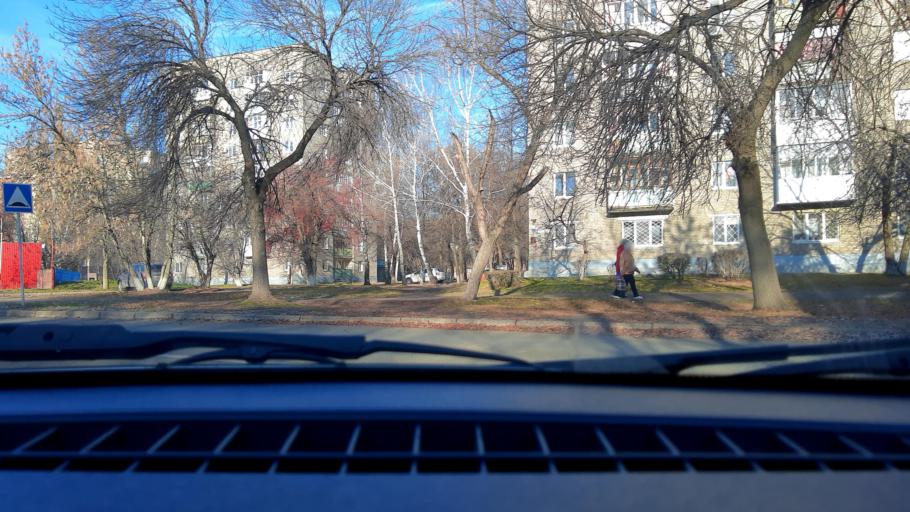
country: RU
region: Bashkortostan
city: Ufa
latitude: 54.8064
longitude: 56.1216
